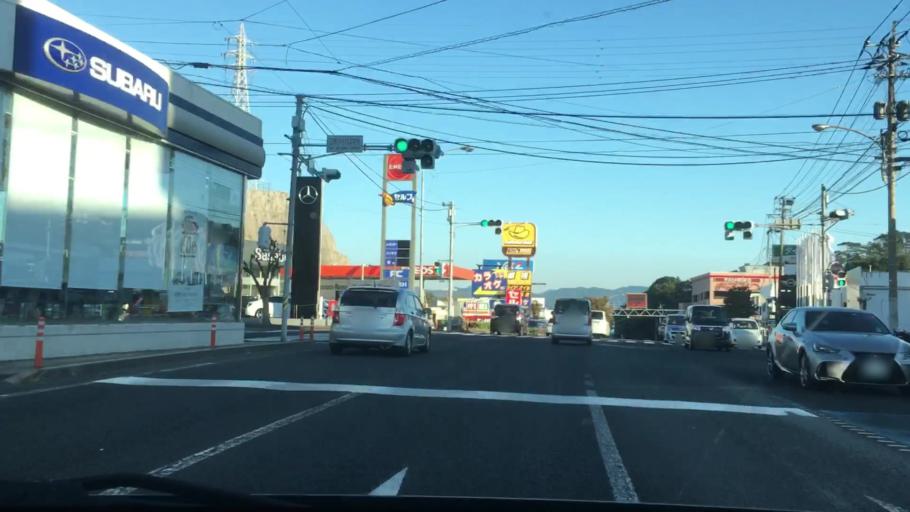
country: JP
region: Nagasaki
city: Sasebo
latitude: 33.1579
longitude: 129.7658
